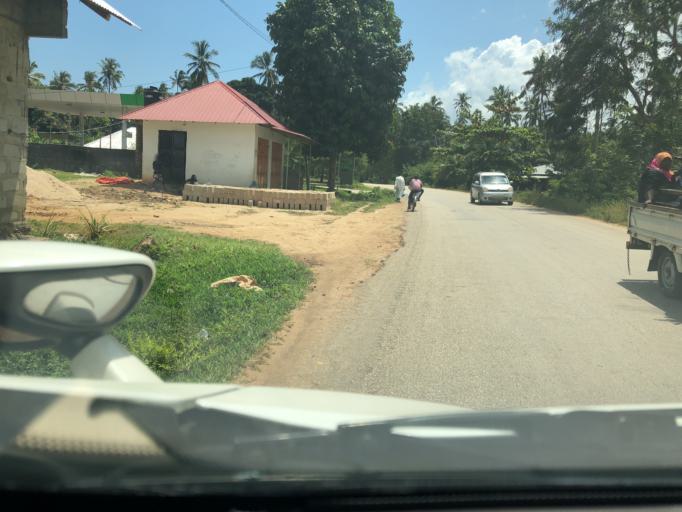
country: TZ
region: Zanzibar Central/South
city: Koani
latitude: -6.0639
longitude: 39.2520
